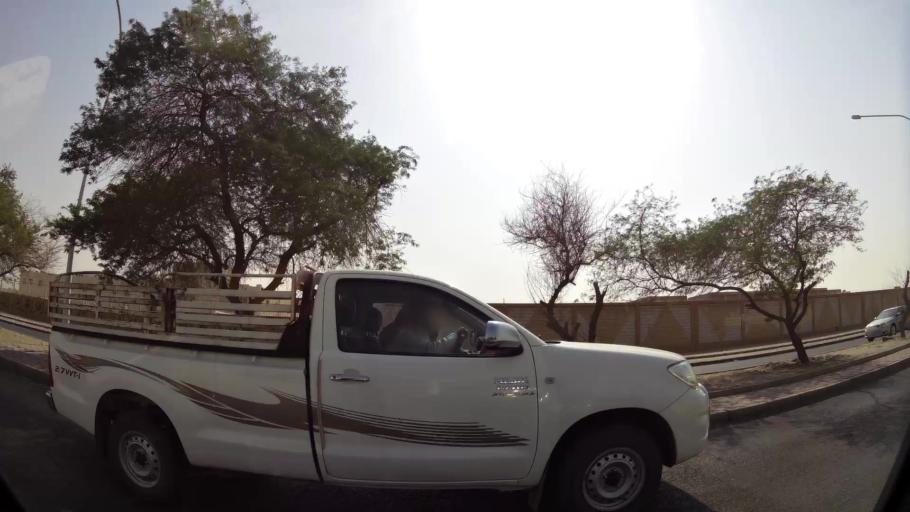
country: KW
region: Muhafazat al Jahra'
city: Al Jahra'
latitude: 29.3315
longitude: 47.6681
